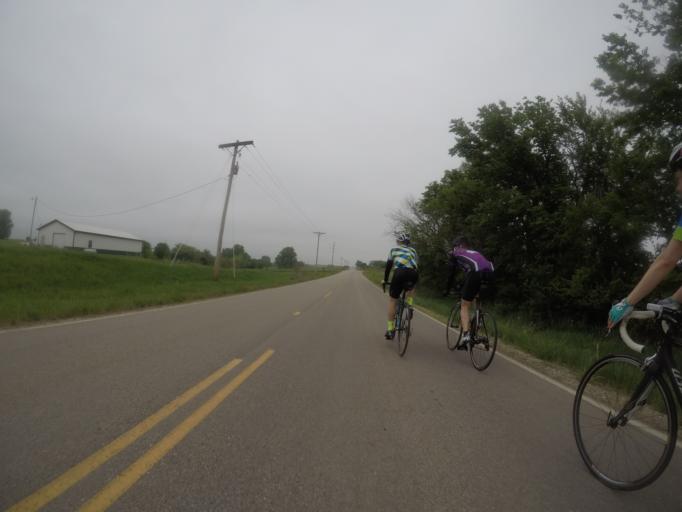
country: US
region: Kansas
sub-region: Pottawatomie County
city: Westmoreland
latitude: 39.5064
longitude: -96.3142
